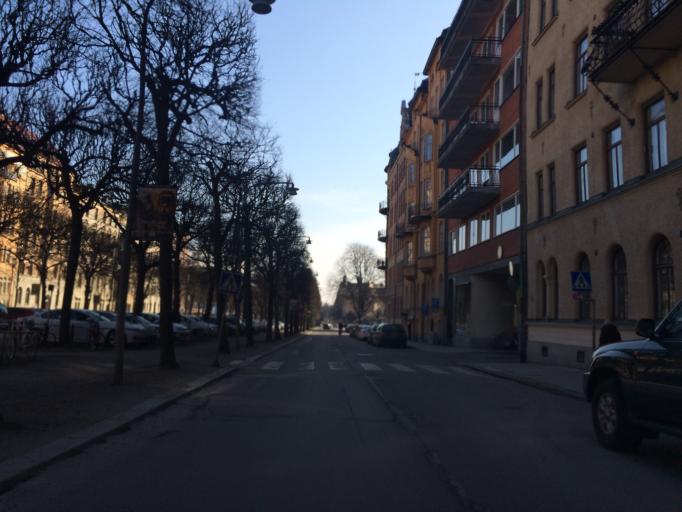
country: SE
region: Stockholm
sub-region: Stockholms Kommun
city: OEstermalm
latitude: 59.3363
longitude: 18.0905
